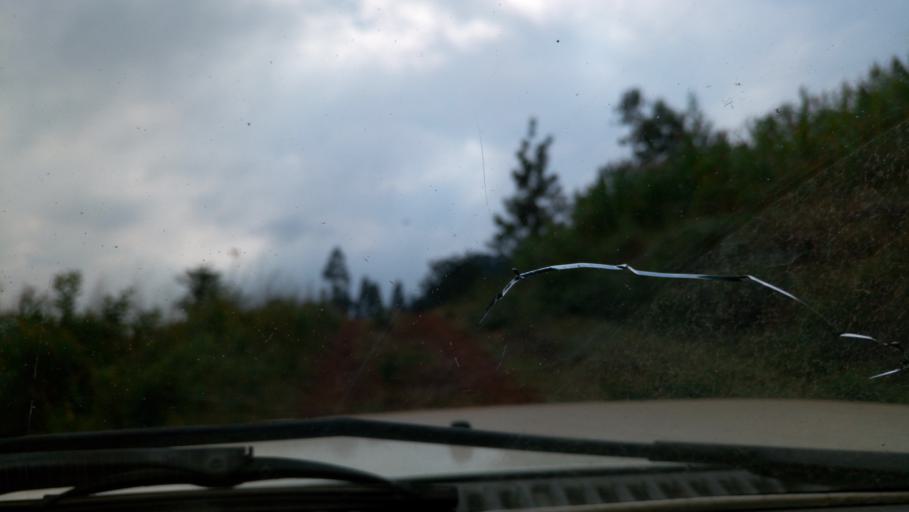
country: KE
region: Murang'a District
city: Kangema
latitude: -0.6283
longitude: 36.9857
